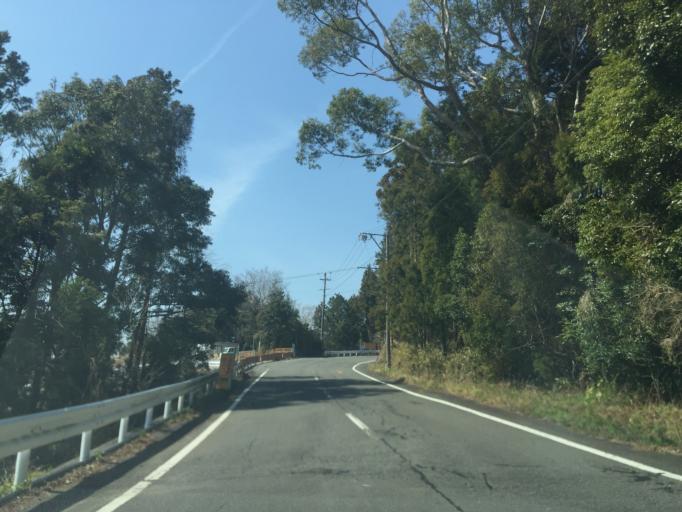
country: JP
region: Shizuoka
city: Kanaya
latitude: 34.8116
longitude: 138.1226
